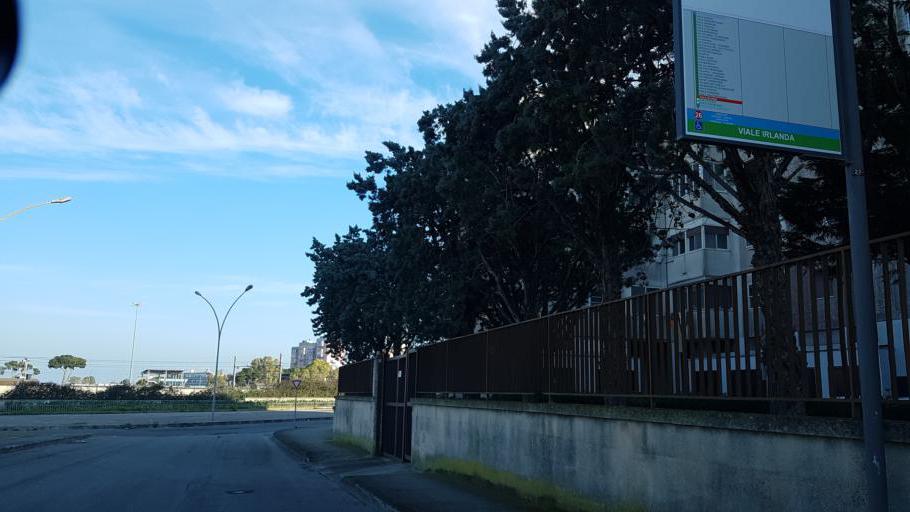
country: IT
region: Apulia
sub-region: Provincia di Brindisi
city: Brindisi
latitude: 40.6246
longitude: 17.9450
